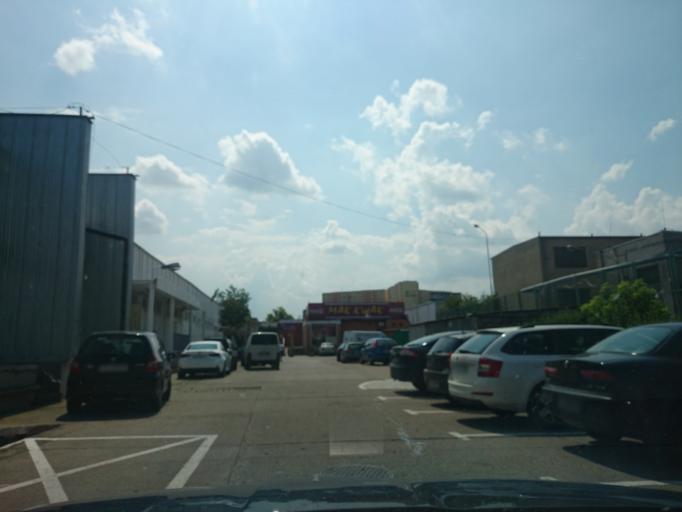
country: PL
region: West Pomeranian Voivodeship
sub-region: Szczecin
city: Szczecin
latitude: 53.3829
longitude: 14.6556
